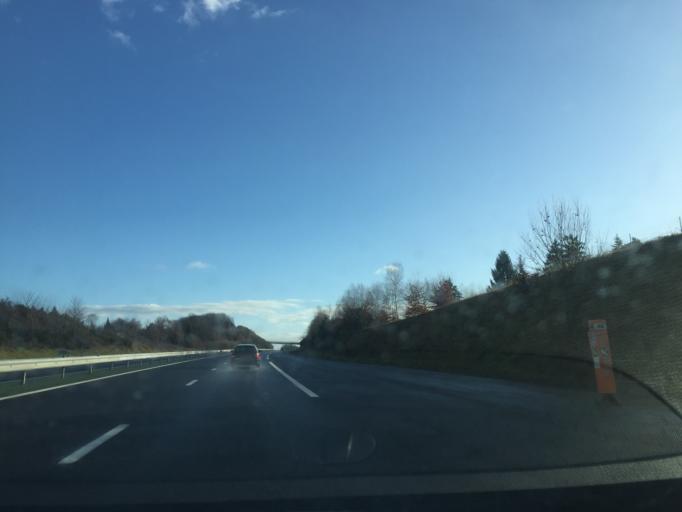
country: FR
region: Limousin
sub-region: Departement de la Correze
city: Saint-Mexant
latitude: 45.3075
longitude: 1.6730
